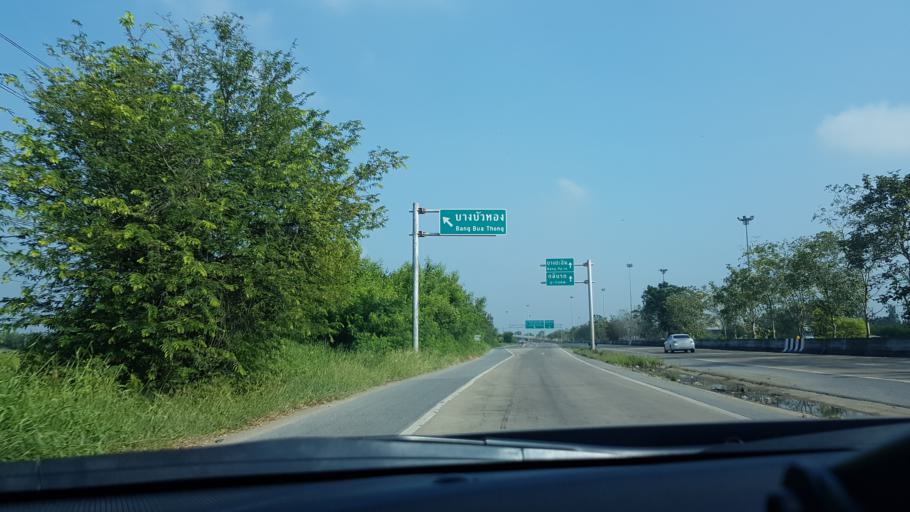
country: TH
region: Phra Nakhon Si Ayutthaya
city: Bang Pa-in
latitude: 14.1492
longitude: 100.5688
